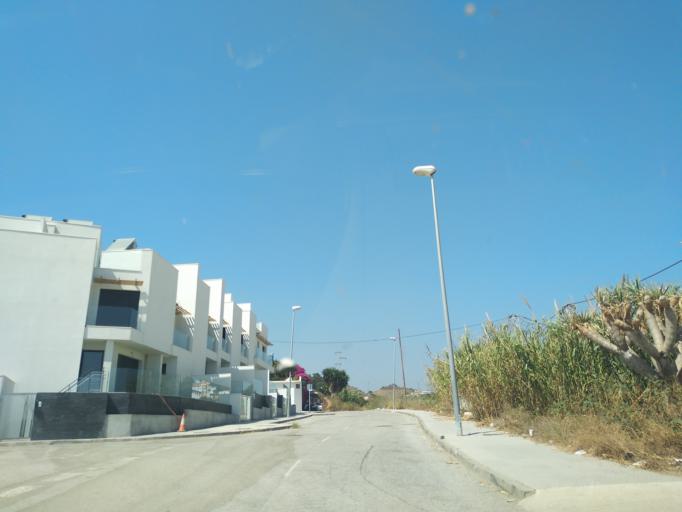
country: ES
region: Andalusia
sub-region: Provincia de Malaga
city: Valdes
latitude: 36.7167
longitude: -4.1943
